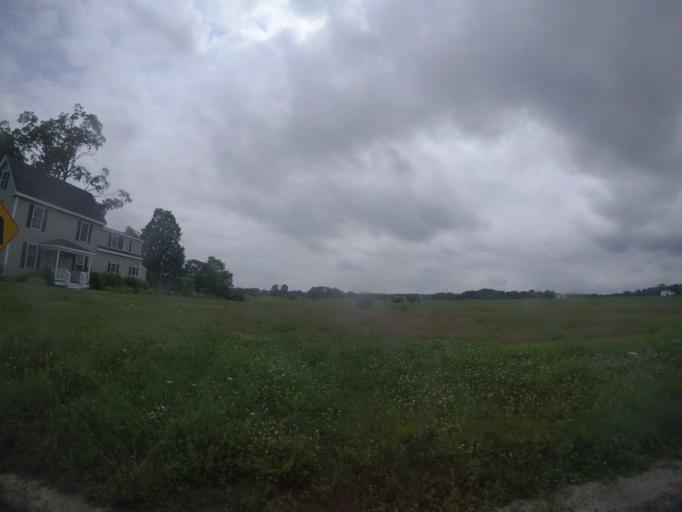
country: US
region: Maine
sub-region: Cumberland County
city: Cumberland Center
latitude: 43.7762
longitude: -70.2566
